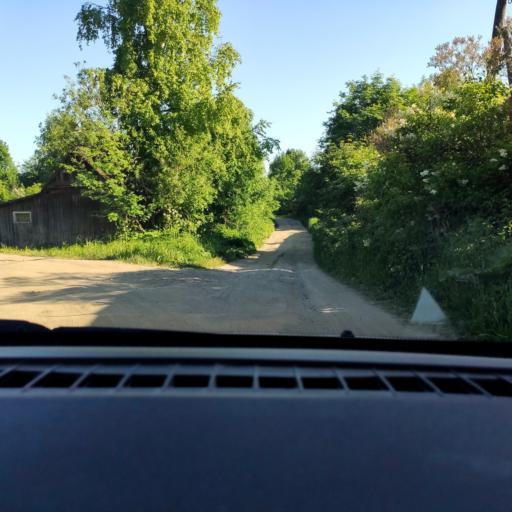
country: RU
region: Perm
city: Overyata
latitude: 58.1205
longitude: 55.8820
